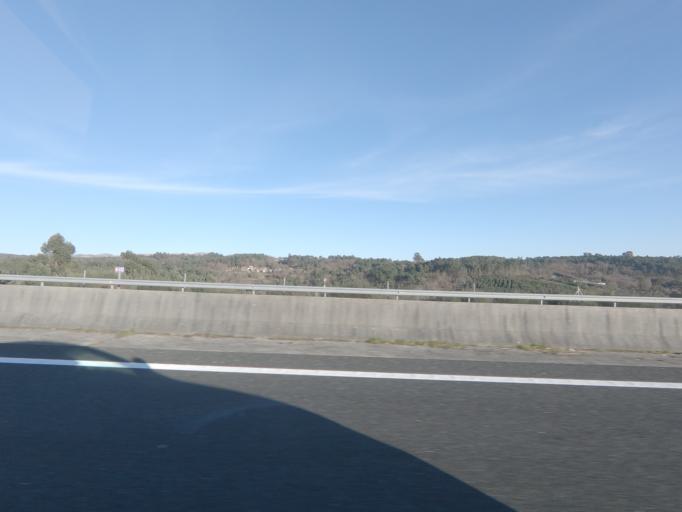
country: ES
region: Galicia
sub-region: Provincia de Ourense
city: Pinor
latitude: 42.5097
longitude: -8.0222
